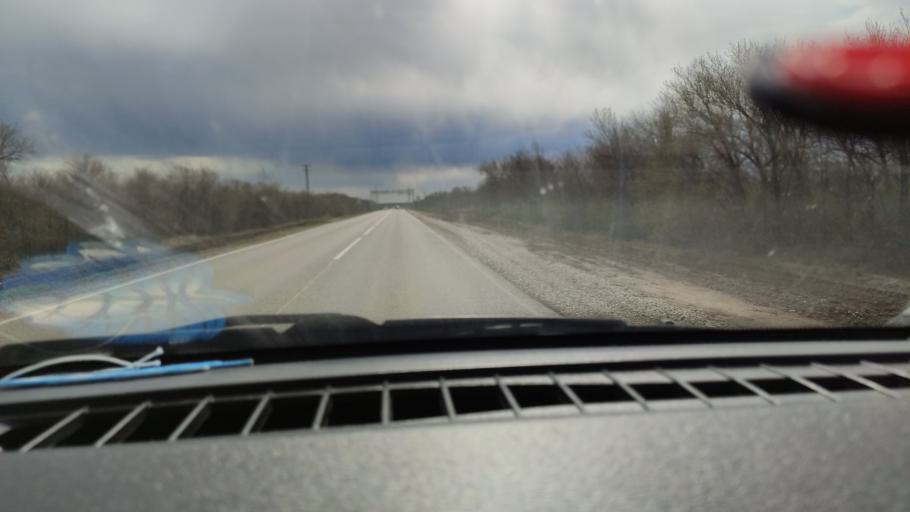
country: RU
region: Saratov
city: Privolzhskiy
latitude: 51.3214
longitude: 46.0258
